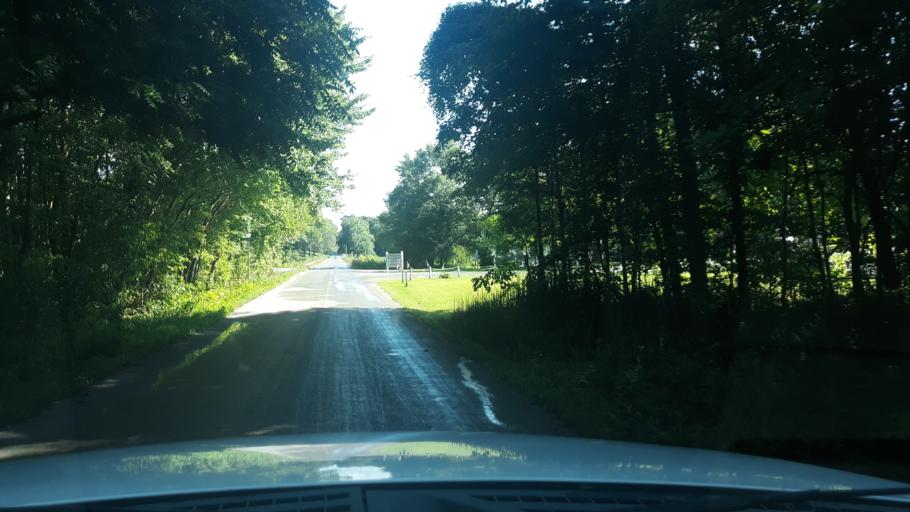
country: US
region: Illinois
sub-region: Saline County
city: Harrisburg
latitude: 37.8569
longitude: -88.5814
